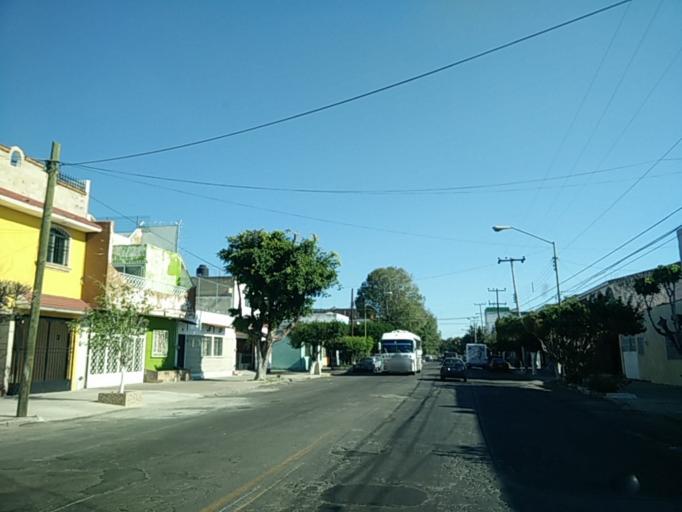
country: MX
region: Jalisco
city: Tlaquepaque
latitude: 20.6552
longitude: -103.3319
